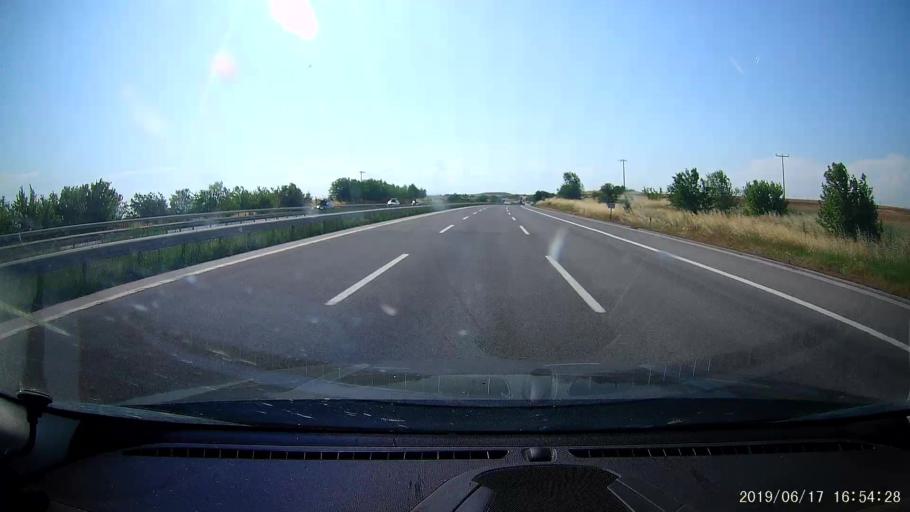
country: TR
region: Kirklareli
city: Inece
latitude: 41.5738
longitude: 26.9948
